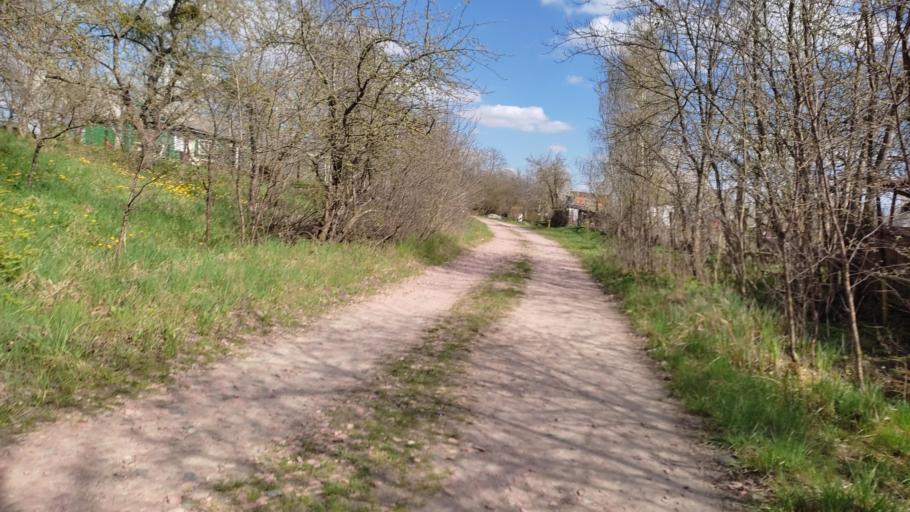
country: BY
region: Grodnenskaya
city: Hrodna
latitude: 53.6566
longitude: 23.9001
